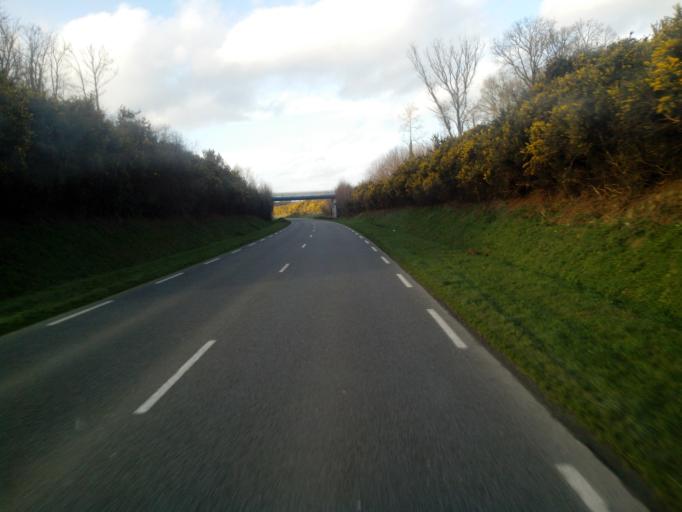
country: FR
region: Brittany
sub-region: Departement des Cotes-d'Armor
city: Pleslin-Trigavou
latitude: 48.5423
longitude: -2.0377
